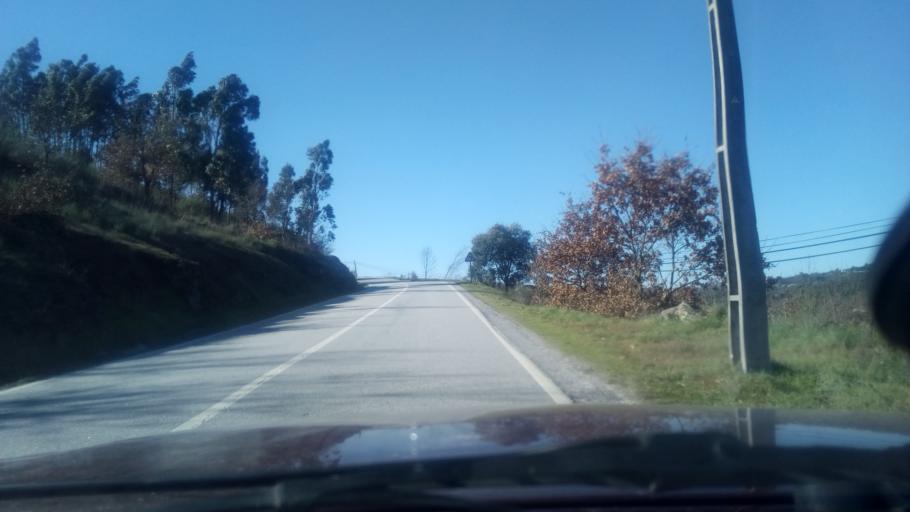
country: PT
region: Guarda
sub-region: Fornos de Algodres
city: Fornos de Algodres
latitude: 40.6096
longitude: -7.5228
